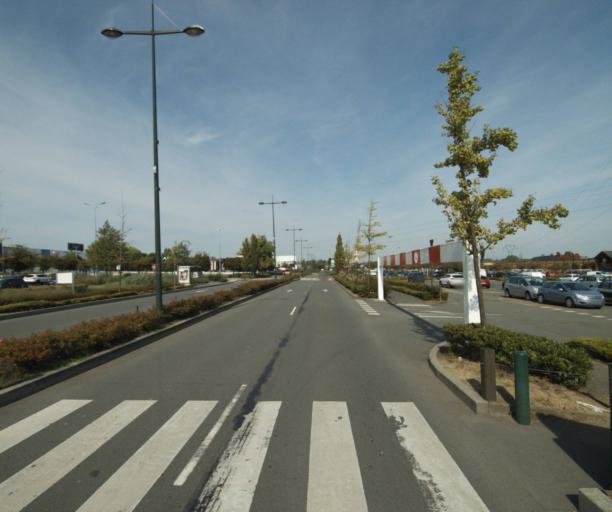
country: FR
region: Nord-Pas-de-Calais
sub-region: Departement du Nord
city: Hallennes-lez-Haubourdin
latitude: 50.6295
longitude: 2.9664
